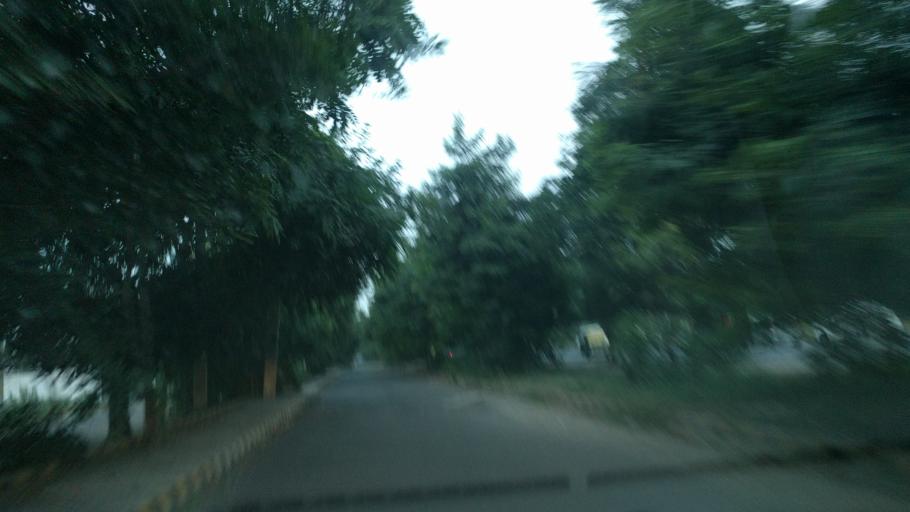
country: IN
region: Haryana
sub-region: Gurgaon
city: Gurgaon
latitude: 28.4512
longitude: 77.0649
